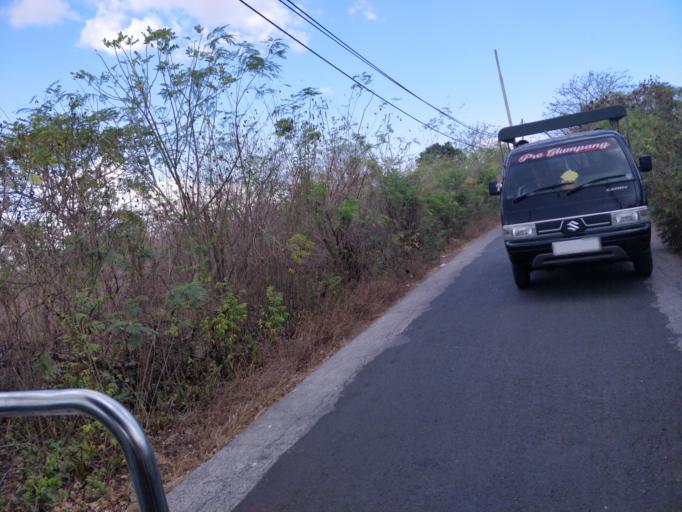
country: ID
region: Bali
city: Jungutbatu Kaja Dua
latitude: -8.6825
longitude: 115.4456
